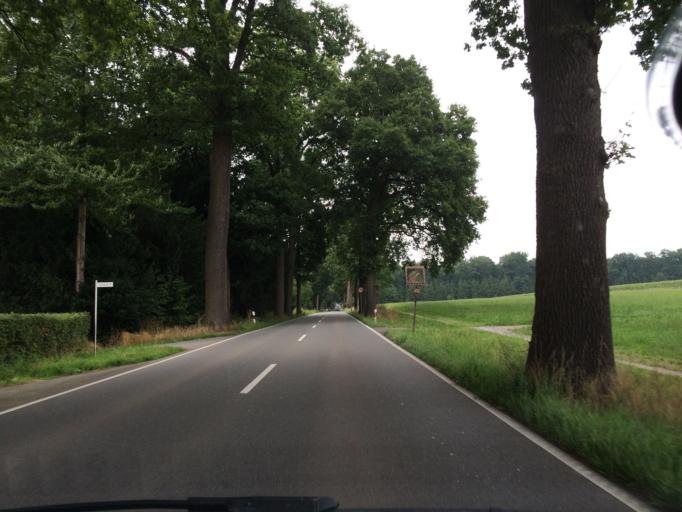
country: DE
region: North Rhine-Westphalia
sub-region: Regierungsbezirk Munster
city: Klein Reken
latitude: 51.7451
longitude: 7.0034
